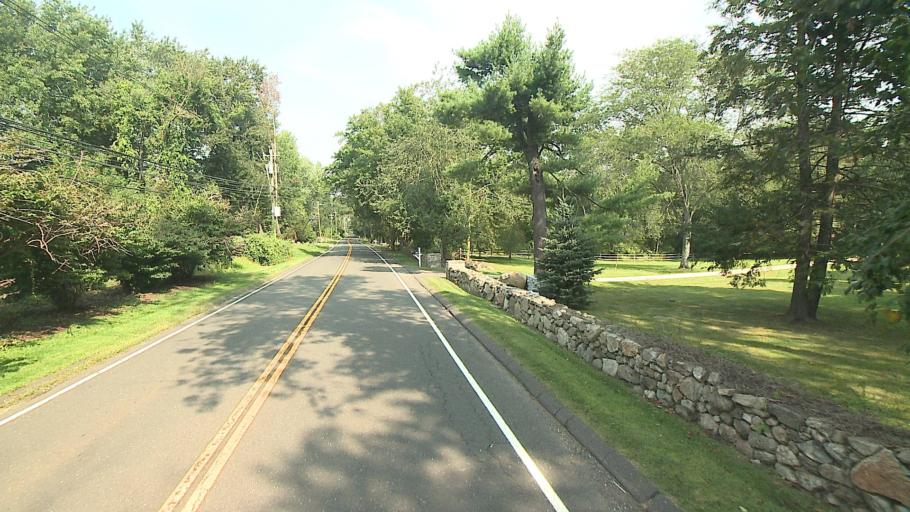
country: US
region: Connecticut
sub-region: Fairfield County
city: Georgetown
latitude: 41.2340
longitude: -73.4051
